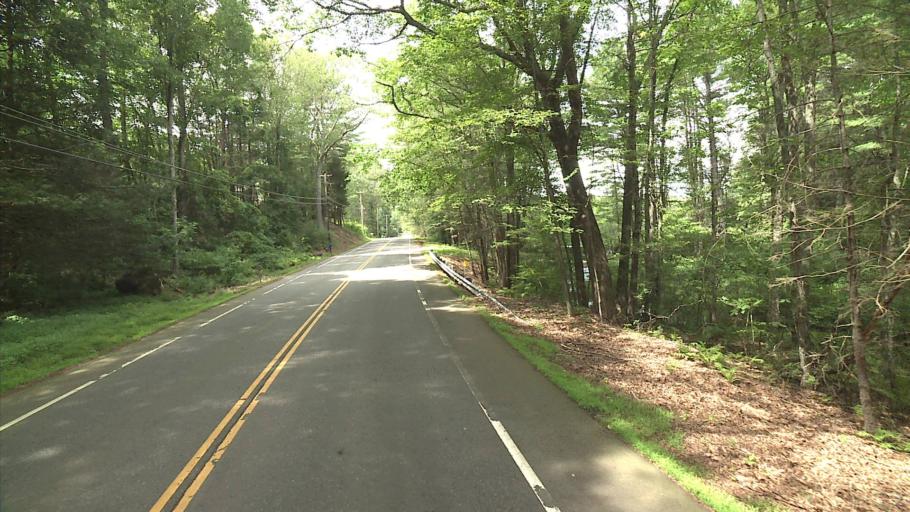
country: US
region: Connecticut
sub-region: Windham County
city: South Woodstock
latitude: 41.9327
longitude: -72.0905
